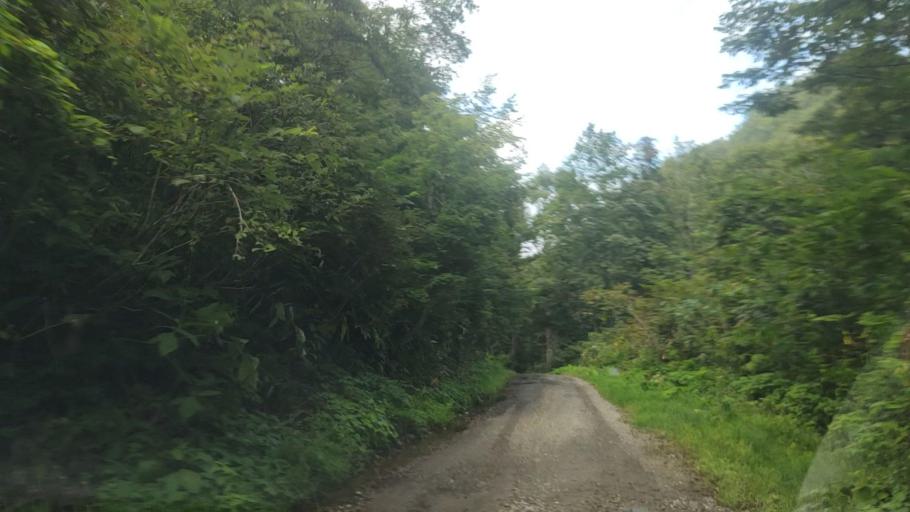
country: JP
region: Toyama
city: Yatsuomachi-higashikumisaka
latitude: 36.3570
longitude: 137.0676
